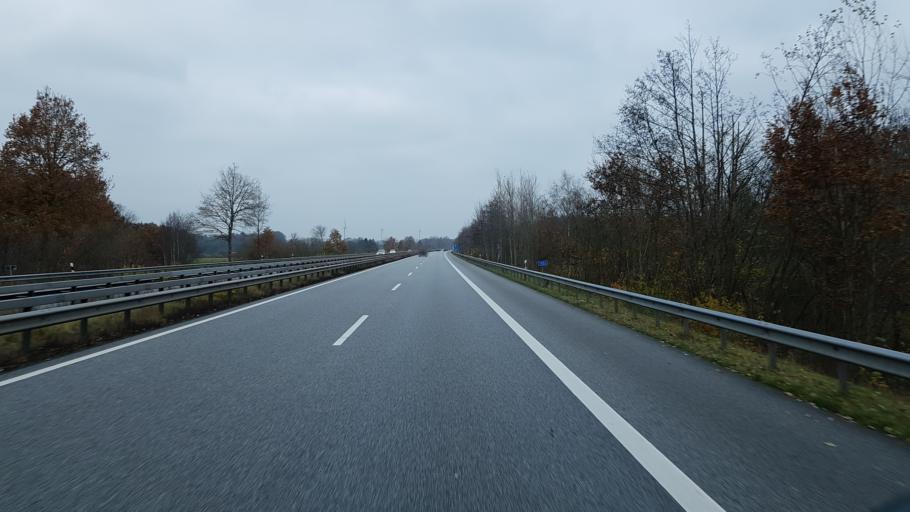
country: DE
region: Lower Saxony
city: Driftsethe
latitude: 53.4246
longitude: 8.5807
